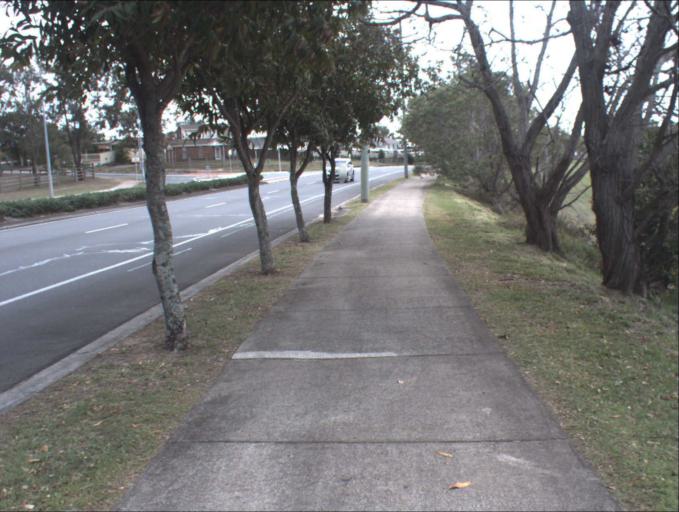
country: AU
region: Queensland
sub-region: Logan
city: Waterford West
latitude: -27.6834
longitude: 153.1375
